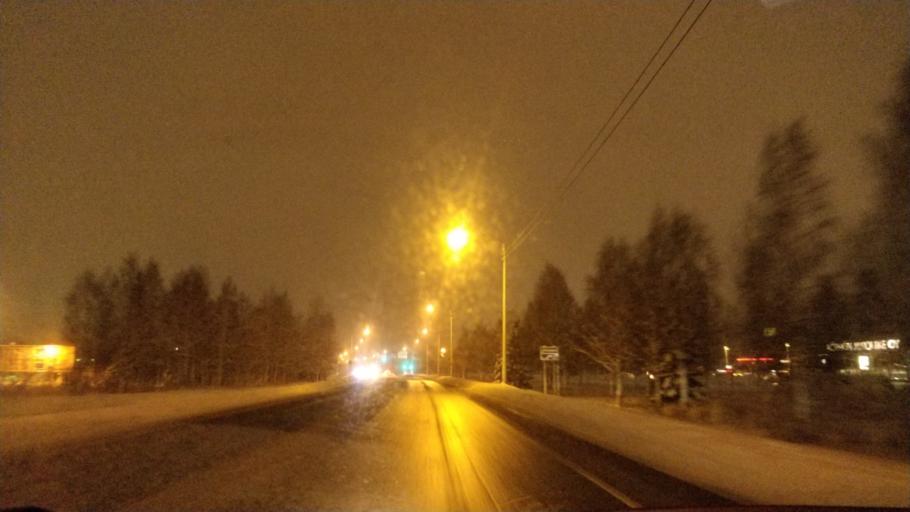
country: FI
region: Lapland
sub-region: Rovaniemi
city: Rovaniemi
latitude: 66.4884
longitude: 25.6622
